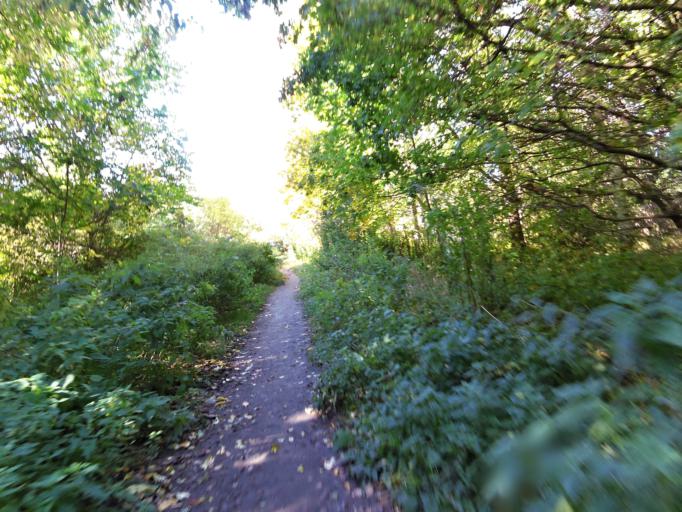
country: DE
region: Saxony
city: Leipzig
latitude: 51.3843
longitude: 12.3686
